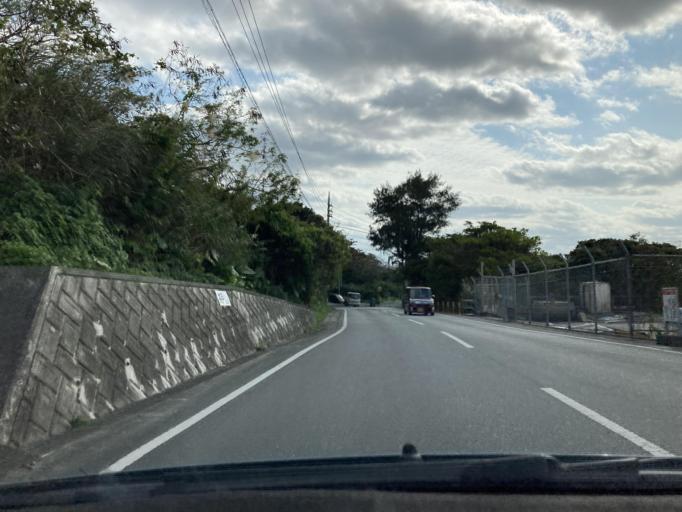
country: JP
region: Okinawa
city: Ginowan
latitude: 26.1866
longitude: 127.7583
